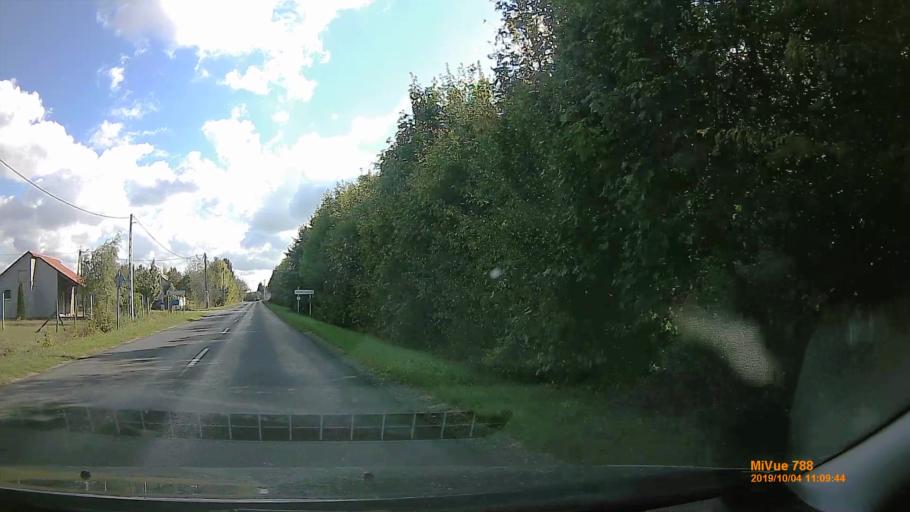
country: HU
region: Somogy
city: Kaposvar
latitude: 46.4134
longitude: 17.7553
